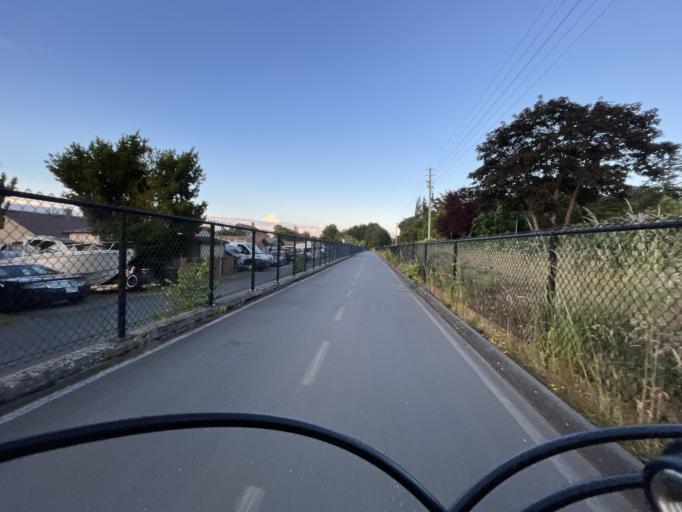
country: CA
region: British Columbia
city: Victoria
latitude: 48.4379
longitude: -123.4101
